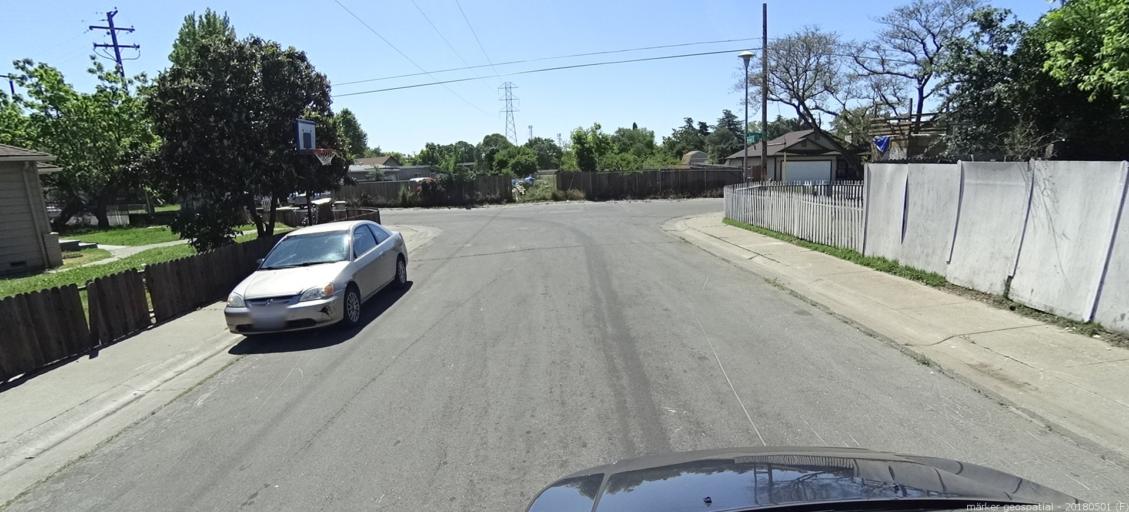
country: US
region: California
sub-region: Sacramento County
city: Rio Linda
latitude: 38.6290
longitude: -121.4390
